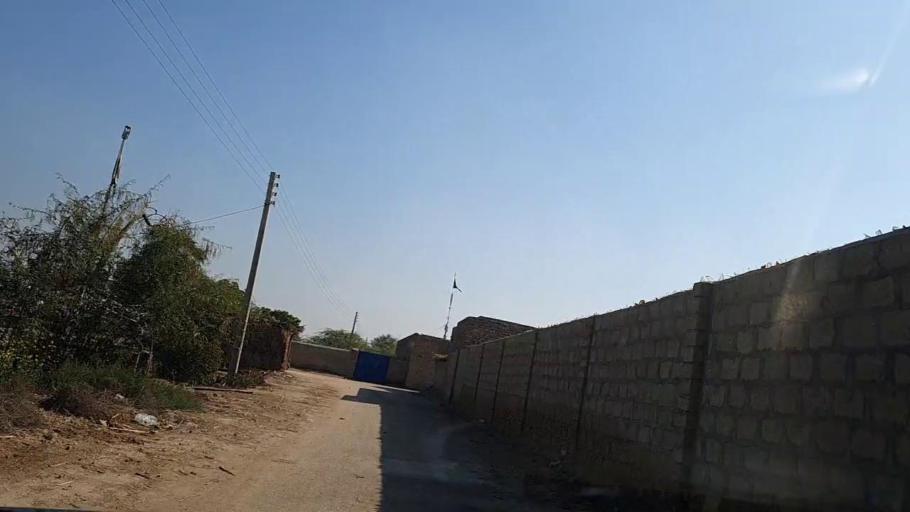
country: PK
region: Sindh
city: Sakrand
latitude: 26.2291
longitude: 68.3106
